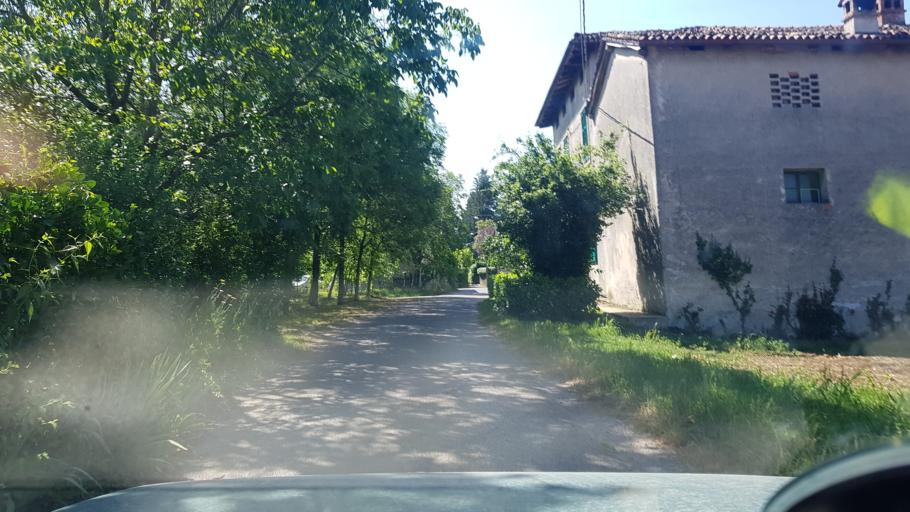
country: SI
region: Nova Gorica
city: Nova Gorica
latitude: 45.9596
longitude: 13.6324
